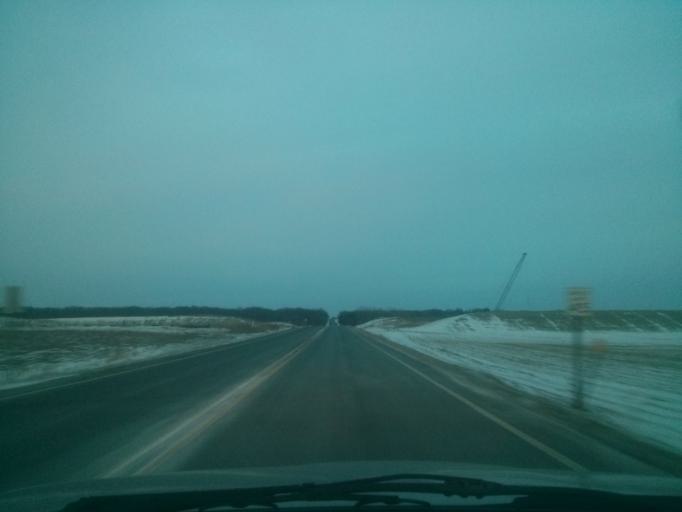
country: US
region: Minnesota
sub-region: Washington County
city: Stillwater
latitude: 45.0607
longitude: -92.7844
